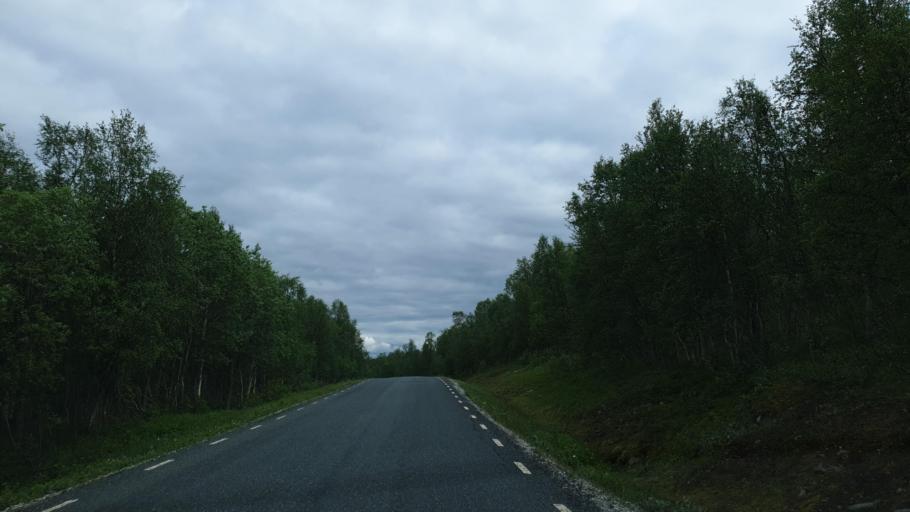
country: NO
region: Nordland
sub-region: Hattfjelldal
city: Hattfjelldal
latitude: 65.4223
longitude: 14.9087
